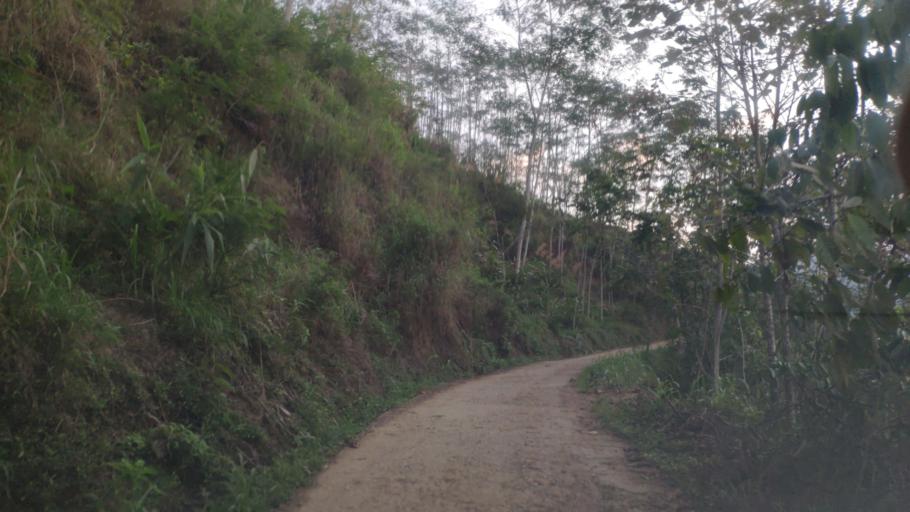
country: ID
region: Central Java
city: Buaran
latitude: -7.2499
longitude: 109.5814
